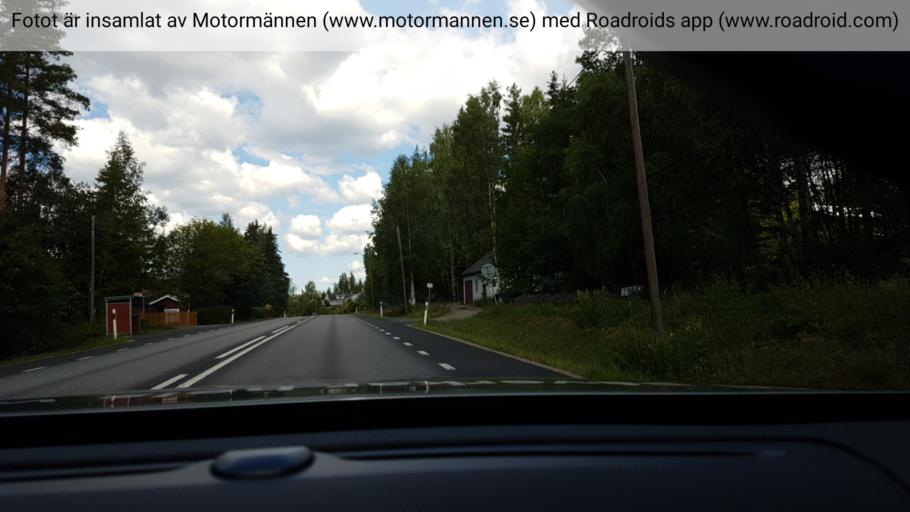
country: SE
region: Dalarna
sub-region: Faluns Kommun
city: Grycksbo
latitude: 60.6930
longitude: 15.4862
